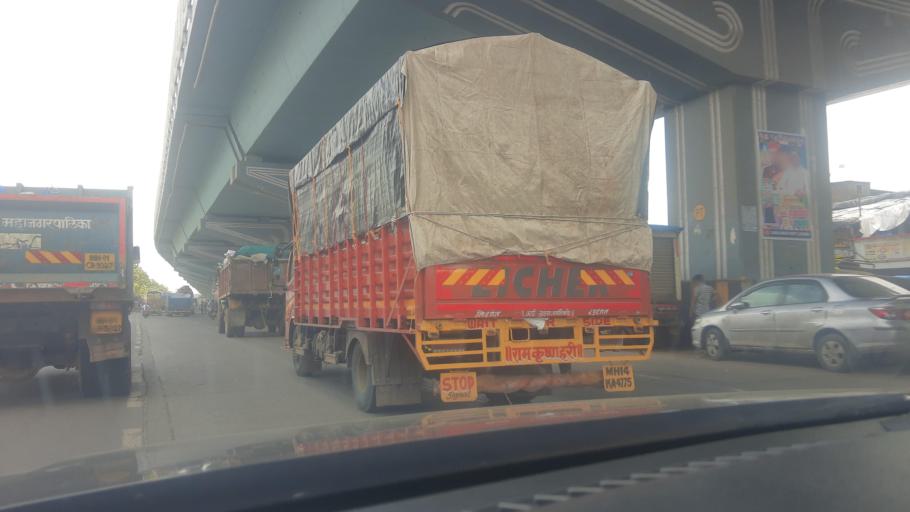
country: IN
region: Maharashtra
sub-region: Mumbai Suburban
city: Mumbai
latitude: 19.0618
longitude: 72.9181
